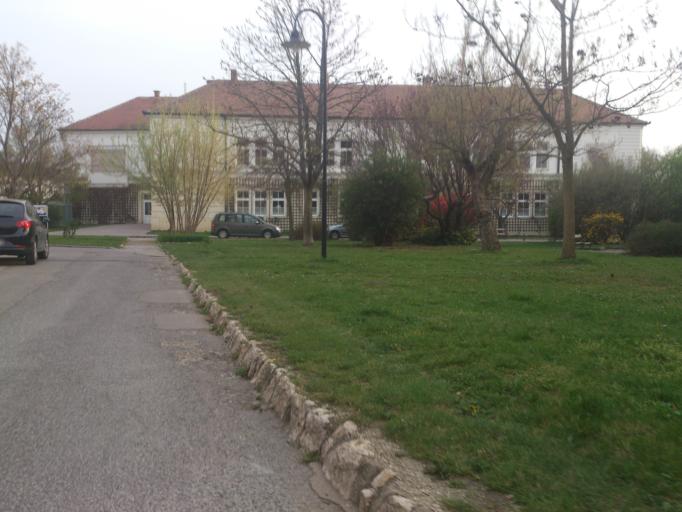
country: AT
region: Lower Austria
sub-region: Politischer Bezirk Mistelbach
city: Wolkersdorf im Weinviertel
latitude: 48.3826
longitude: 16.5198
